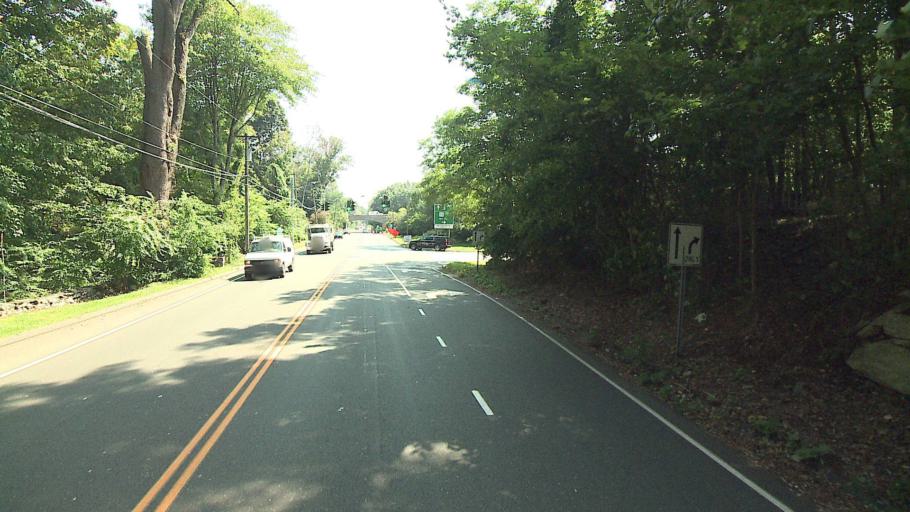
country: US
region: Connecticut
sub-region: Fairfield County
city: Westport
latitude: 41.1654
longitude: -73.3591
